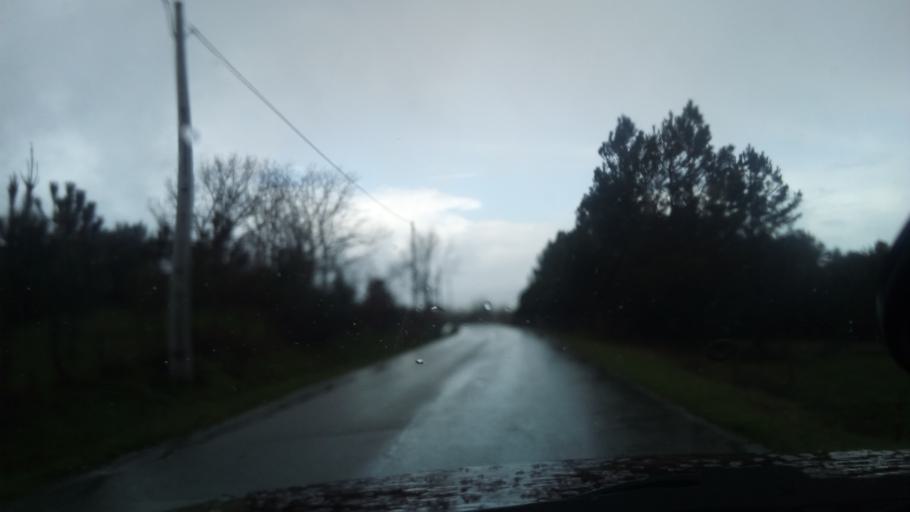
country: PT
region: Guarda
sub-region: Celorico da Beira
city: Celorico da Beira
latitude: 40.5513
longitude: -7.4596
